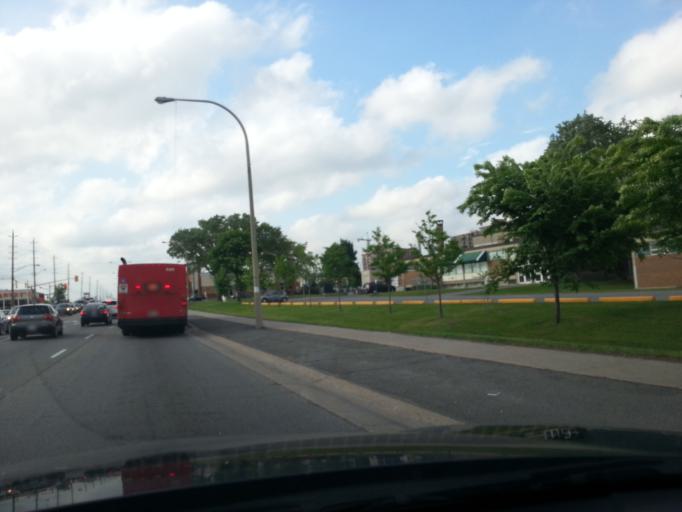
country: CA
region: Ontario
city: Ottawa
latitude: 45.3428
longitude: -75.7287
